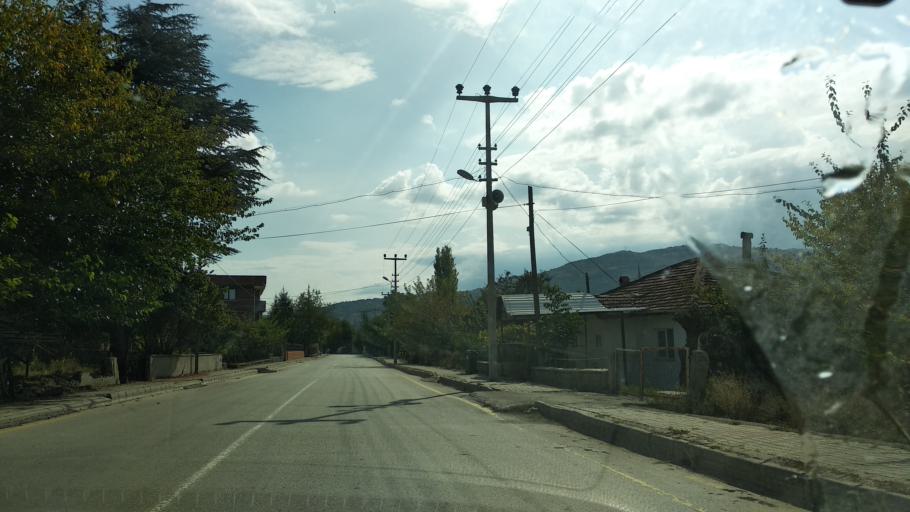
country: TR
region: Bolu
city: Seben
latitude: 40.4112
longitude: 31.5698
